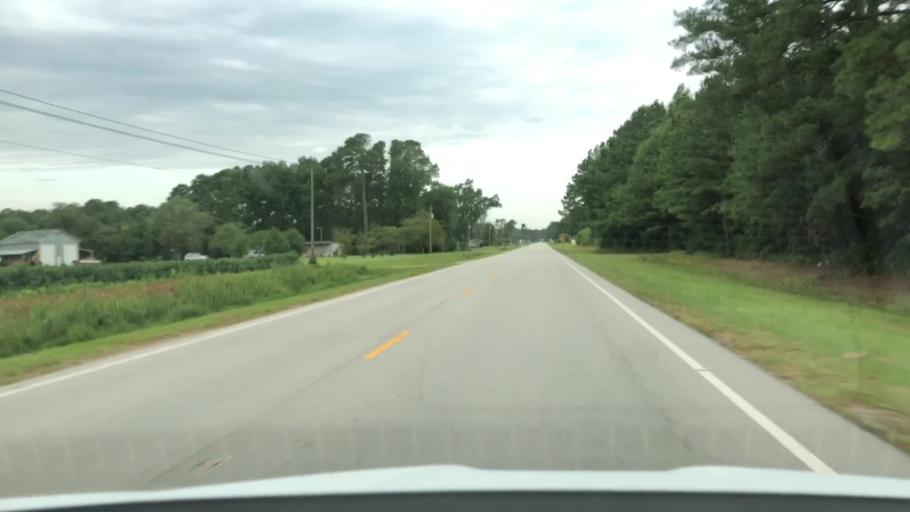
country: US
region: North Carolina
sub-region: Jones County
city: Trenton
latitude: 35.0337
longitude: -77.3236
